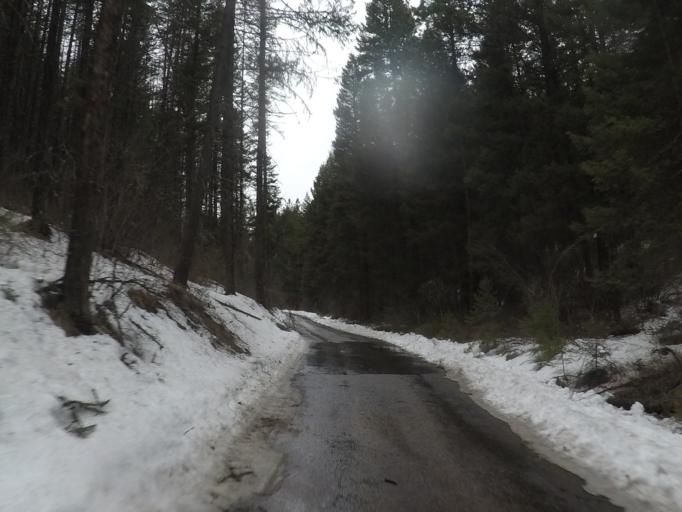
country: US
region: Montana
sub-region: Missoula County
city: Missoula
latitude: 46.9295
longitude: -113.9686
